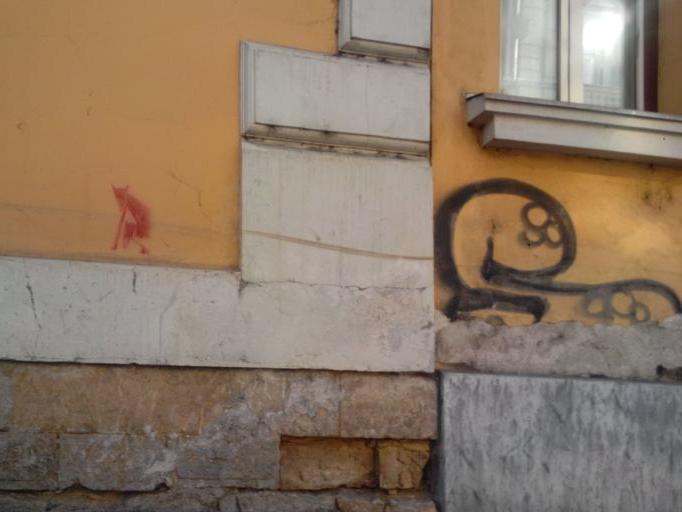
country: RO
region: Cluj
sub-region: Municipiul Cluj-Napoca
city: Cluj-Napoca
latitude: 46.7730
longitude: 23.5965
